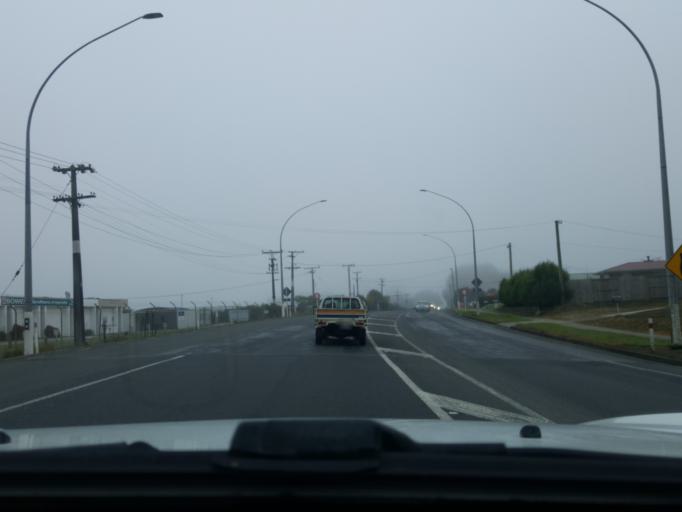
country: NZ
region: Waikato
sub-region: Waikato District
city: Ngaruawahia
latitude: -37.7020
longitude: 175.1995
